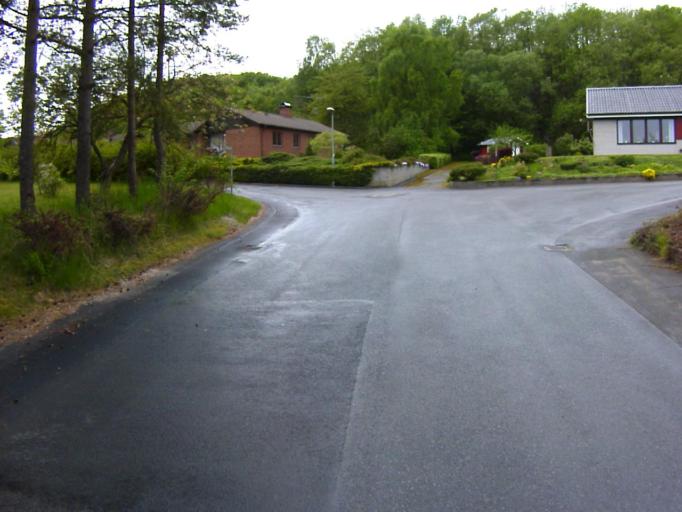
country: SE
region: Skane
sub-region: Kristianstads Kommun
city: Degeberga
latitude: 55.8286
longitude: 14.0793
